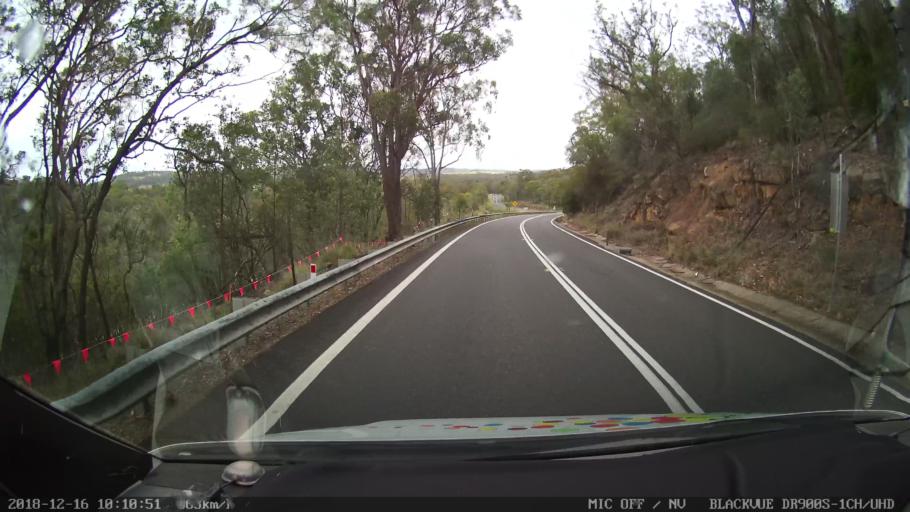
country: AU
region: New South Wales
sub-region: Glen Innes Severn
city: Glen Innes
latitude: -29.3158
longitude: 151.9280
